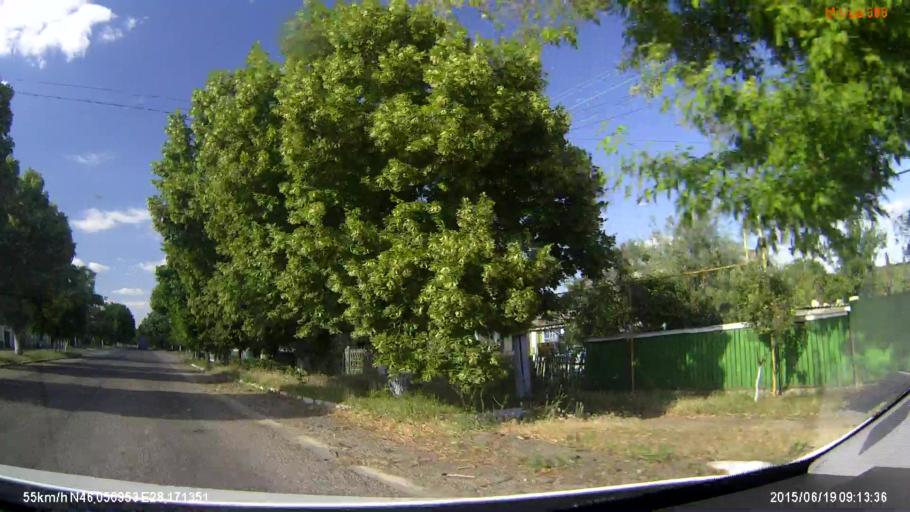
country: RO
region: Vaslui
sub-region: Oras Murgeni
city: Carja
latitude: 46.0508
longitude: 28.1713
